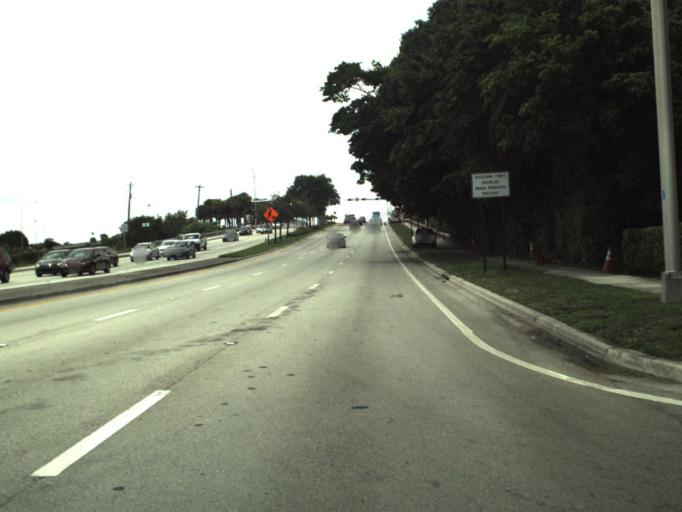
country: US
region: Florida
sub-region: Broward County
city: Coconut Creek
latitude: 26.2315
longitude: -80.1742
